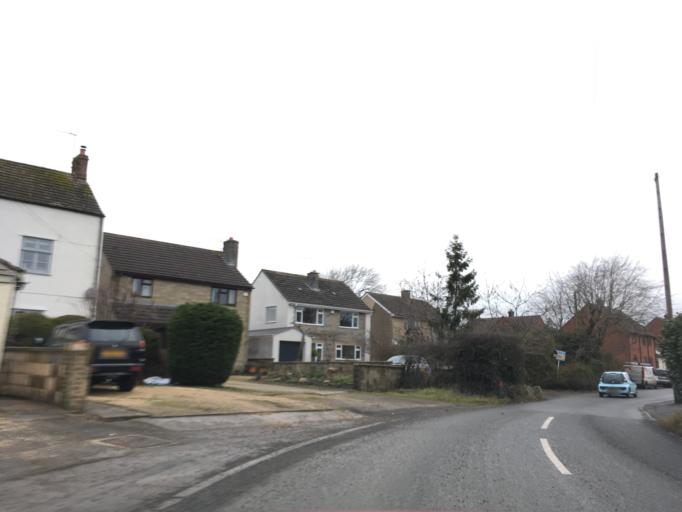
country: GB
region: England
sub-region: Gloucestershire
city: Wotton-under-Edge
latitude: 51.6215
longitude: -2.3677
